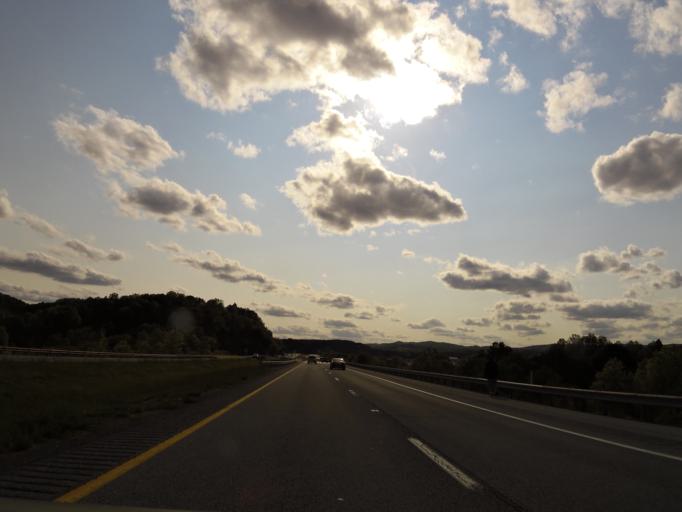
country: US
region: West Virginia
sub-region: Mercer County
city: Princeton
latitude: 37.3605
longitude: -81.0839
